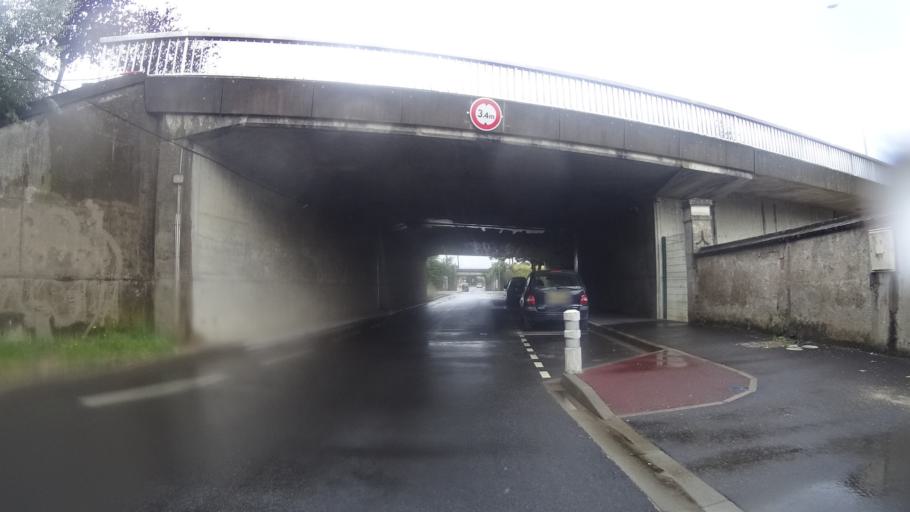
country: FR
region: Centre
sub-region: Departement du Loiret
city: Saint-Jean-le-Blanc
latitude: 47.8934
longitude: 1.9213
